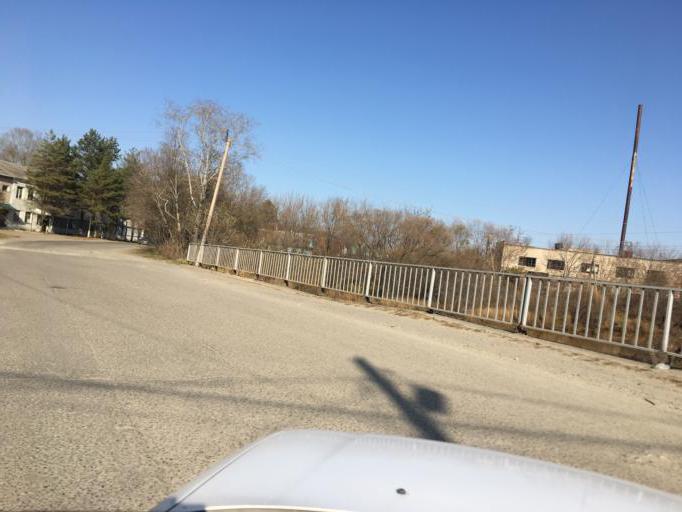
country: RU
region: Primorskiy
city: Dal'nerechensk
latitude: 45.9249
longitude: 133.7263
